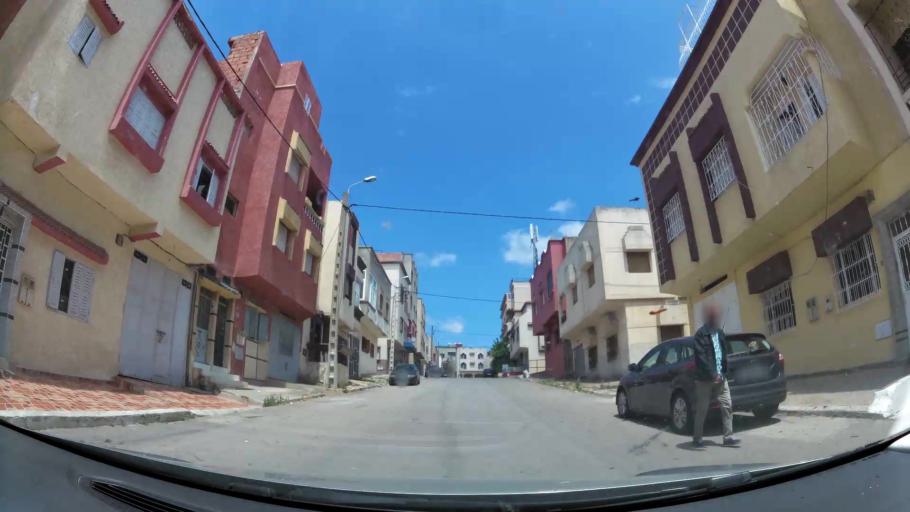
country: MA
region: Gharb-Chrarda-Beni Hssen
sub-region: Kenitra Province
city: Kenitra
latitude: 34.2738
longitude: -6.6007
